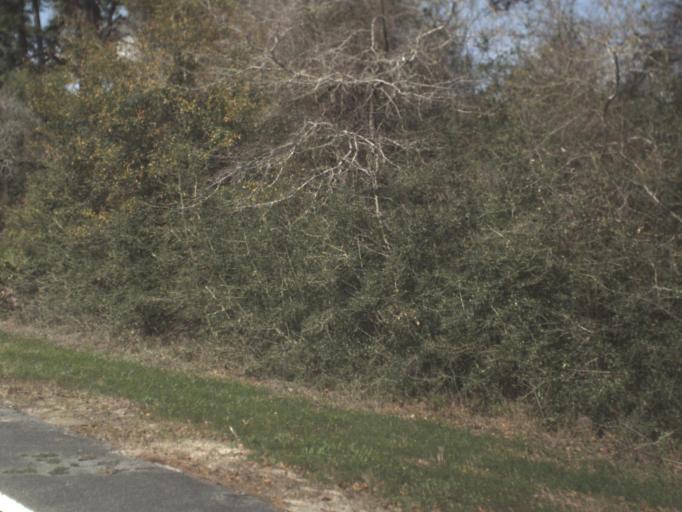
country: US
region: Florida
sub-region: Franklin County
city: Carrabelle
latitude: 29.9520
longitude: -84.5041
